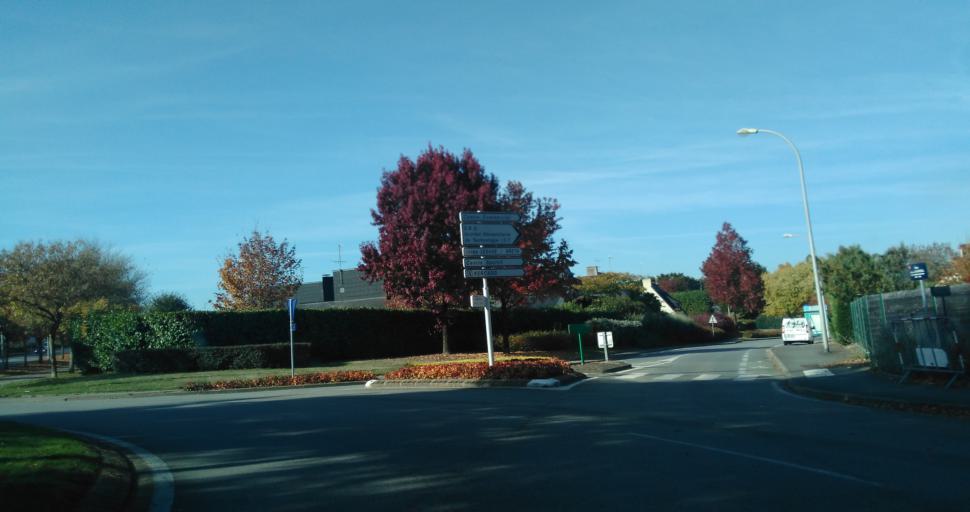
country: FR
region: Brittany
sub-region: Departement du Morbihan
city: Vannes
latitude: 47.6415
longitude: -2.7709
